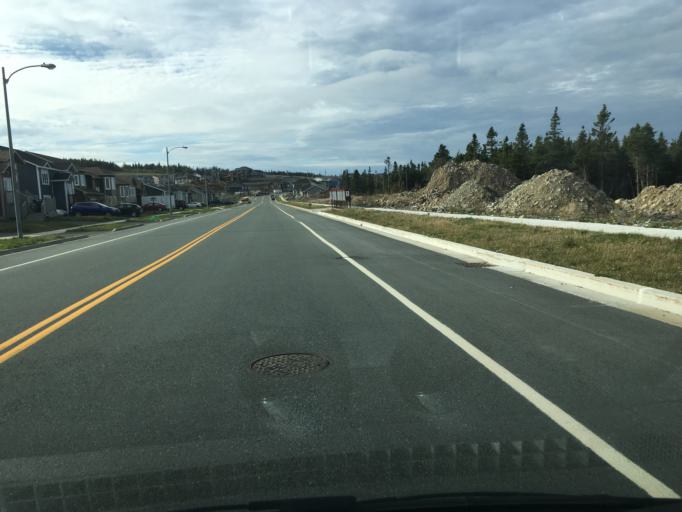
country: CA
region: Newfoundland and Labrador
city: Mount Pearl
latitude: 47.5549
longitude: -52.7929
